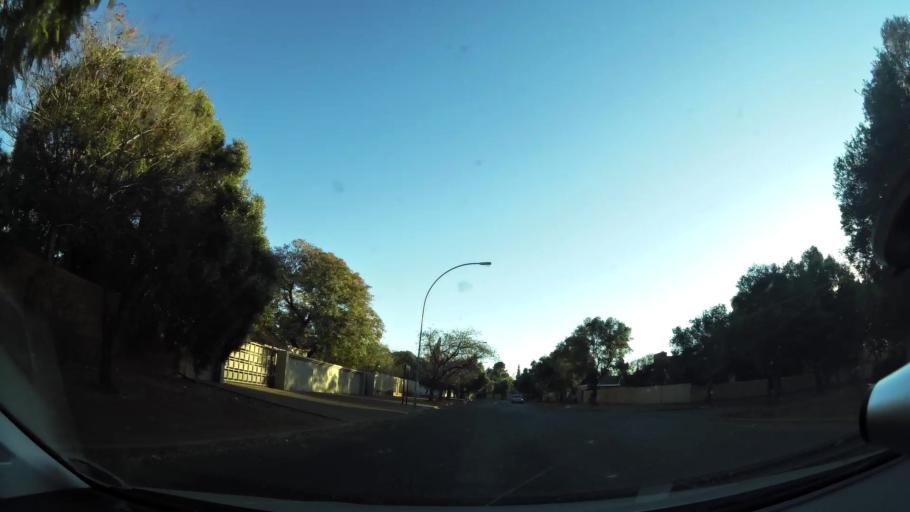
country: ZA
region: Northern Cape
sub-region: Frances Baard District Municipality
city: Kimberley
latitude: -28.7594
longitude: 24.7659
